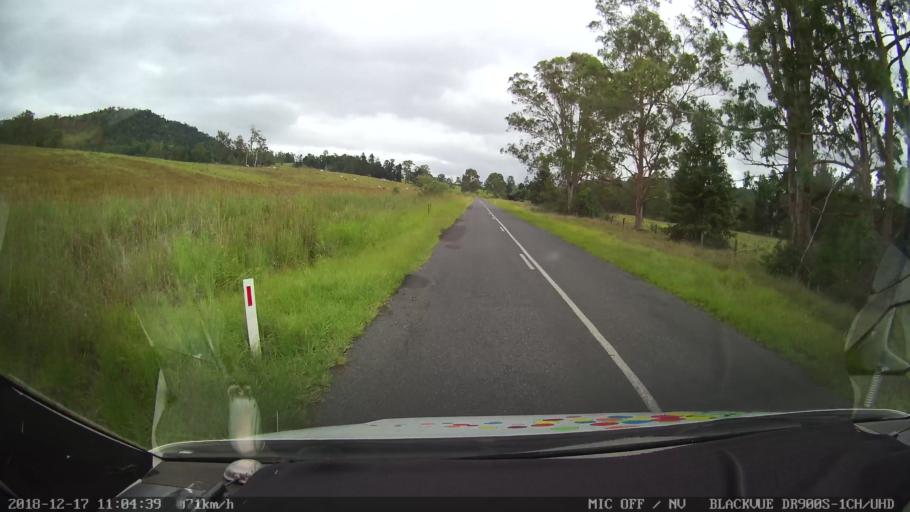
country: AU
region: New South Wales
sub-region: Kyogle
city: Kyogle
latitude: -28.7968
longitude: 152.6433
